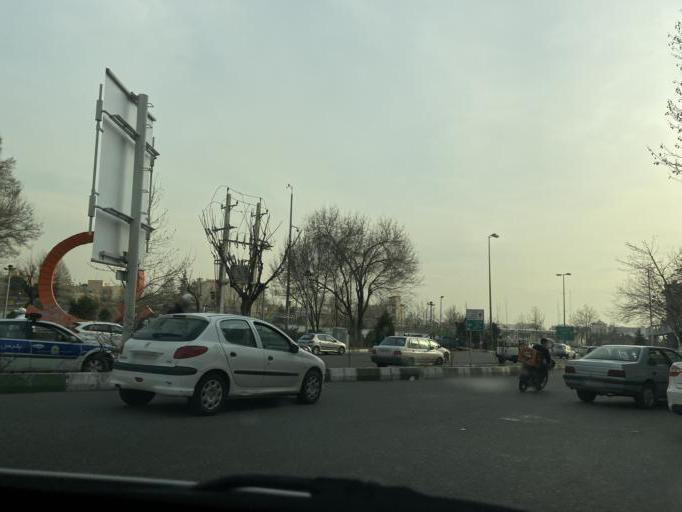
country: IR
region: Tehran
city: Tajrish
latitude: 35.8021
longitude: 51.4863
